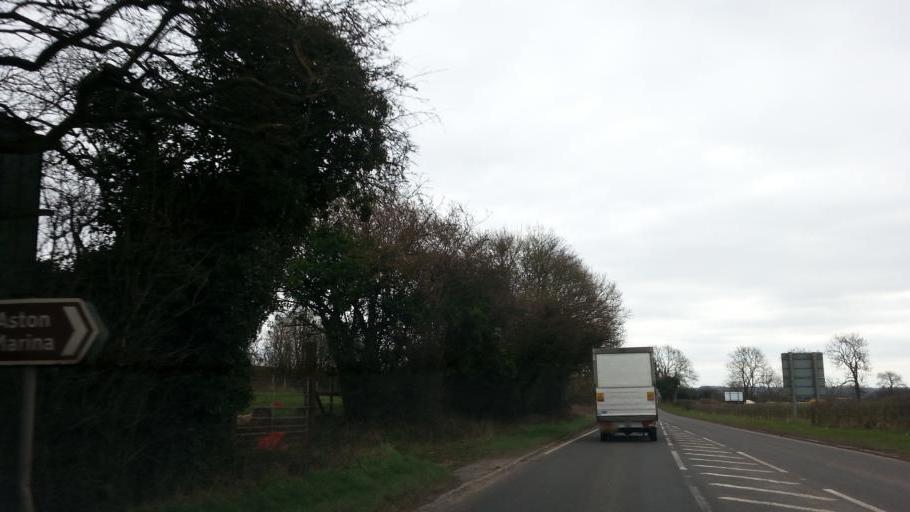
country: GB
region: England
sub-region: Staffordshire
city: Stone
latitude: 52.8860
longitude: -2.1202
